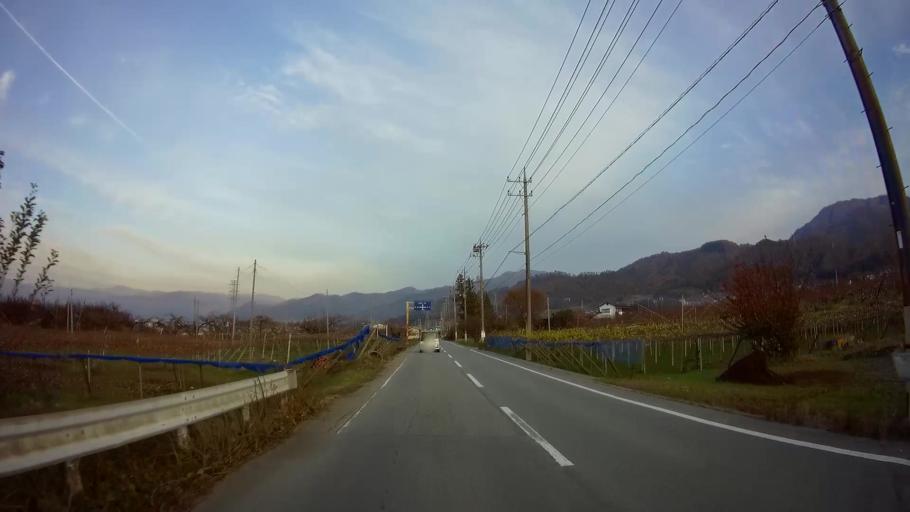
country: JP
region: Yamanashi
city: Isawa
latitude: 35.6125
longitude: 138.6611
